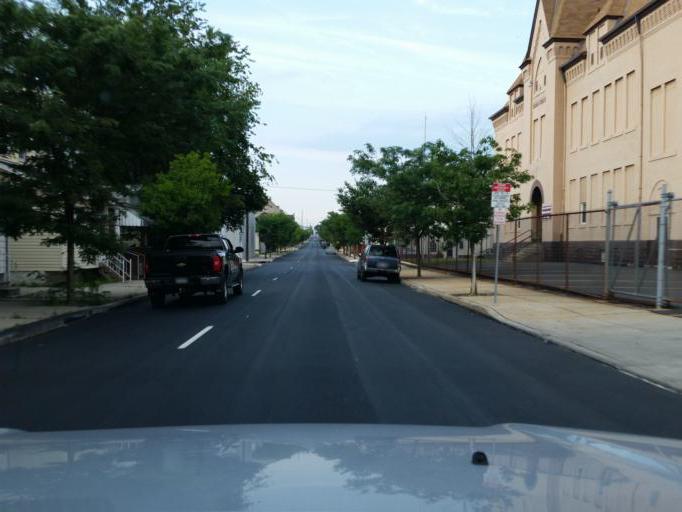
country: US
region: Pennsylvania
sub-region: Blair County
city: Altoona
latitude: 40.5017
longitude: -78.4058
